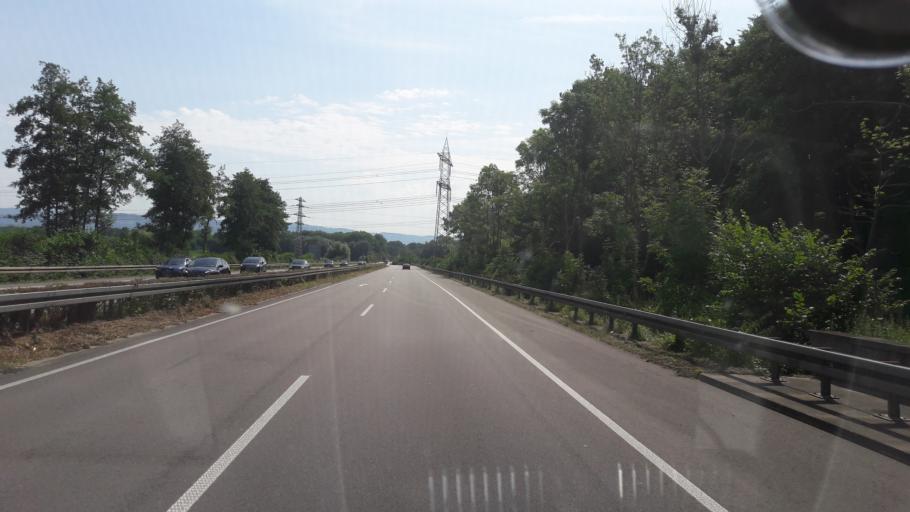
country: DE
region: Baden-Wuerttemberg
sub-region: Freiburg Region
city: Appenweier
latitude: 48.5340
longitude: 7.9431
